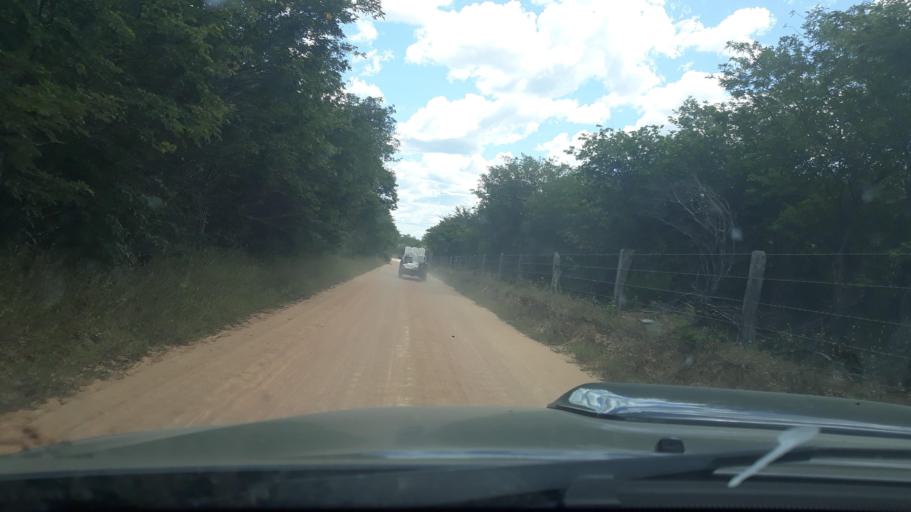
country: BR
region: Bahia
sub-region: Riacho De Santana
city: Riacho de Santana
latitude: -13.9078
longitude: -42.9331
